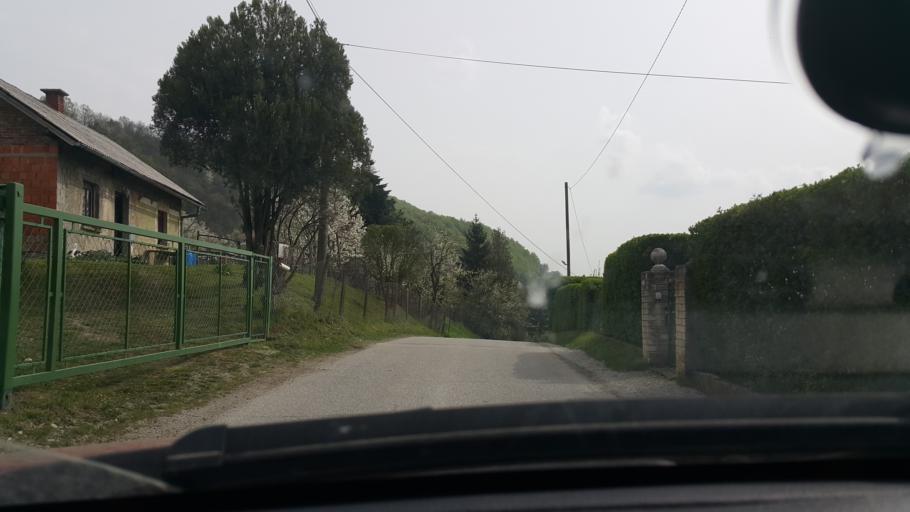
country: SI
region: Duplek
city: Zgornji Duplek
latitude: 46.5351
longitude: 15.7208
